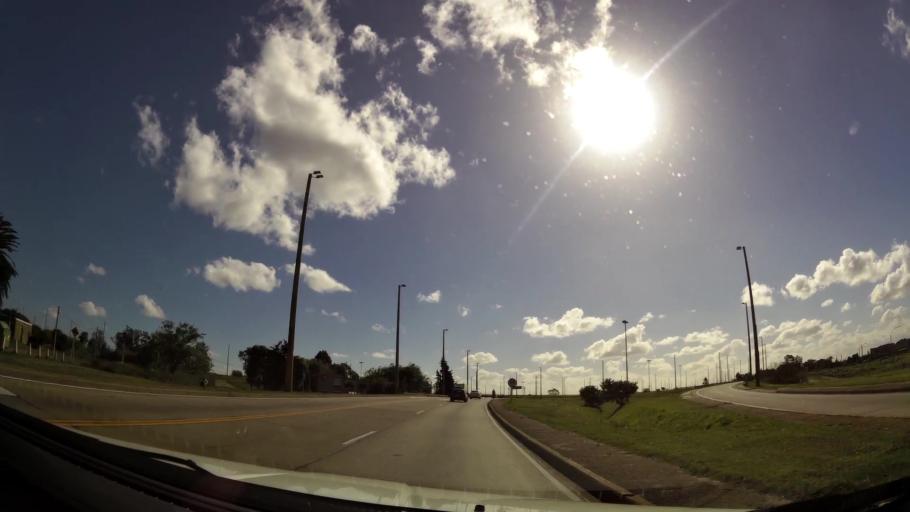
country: UY
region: Canelones
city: La Paz
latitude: -34.8240
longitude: -56.2444
